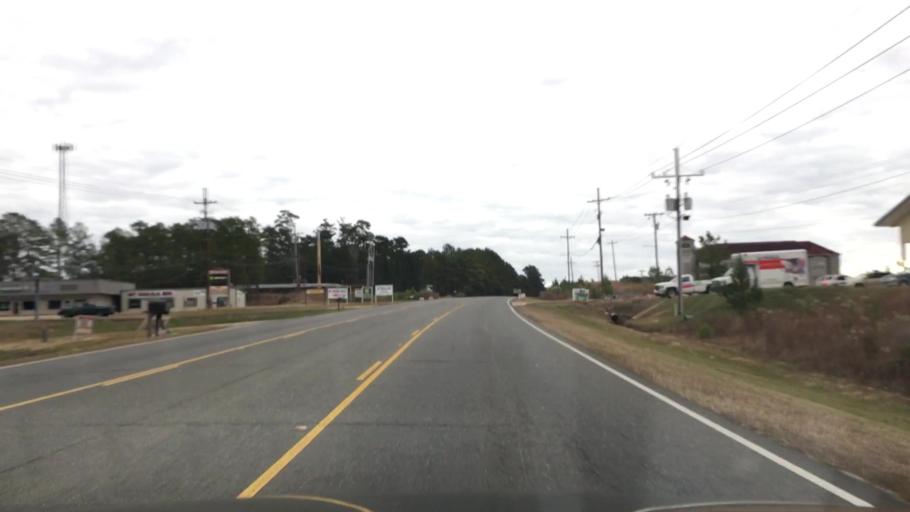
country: US
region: Louisiana
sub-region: Vernon Parish
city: Fort Polk South
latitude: 31.0550
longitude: -93.2425
